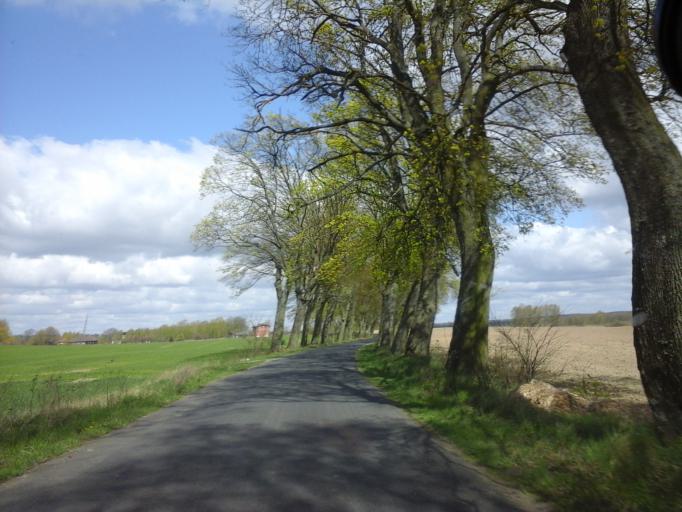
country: PL
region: West Pomeranian Voivodeship
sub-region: Powiat choszczenski
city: Recz
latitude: 53.1688
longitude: 15.6103
